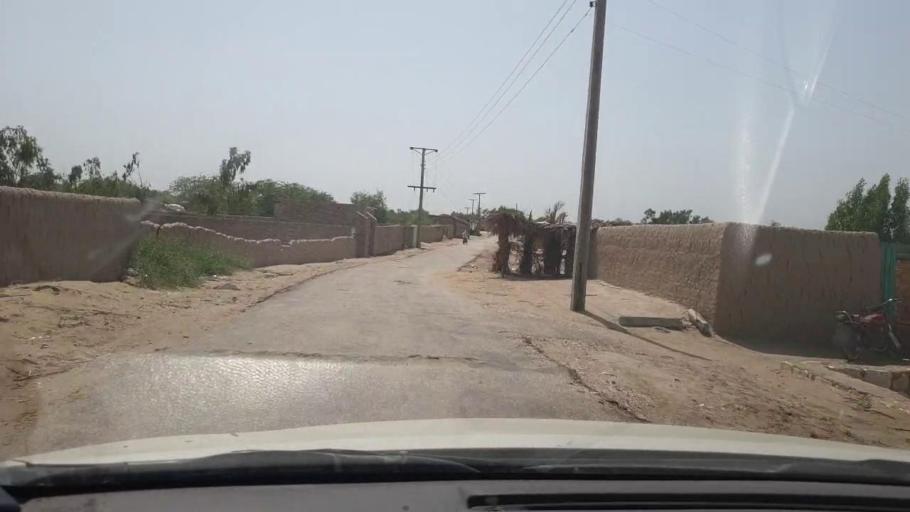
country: PK
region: Sindh
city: Rohri
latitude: 27.5220
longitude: 69.0565
